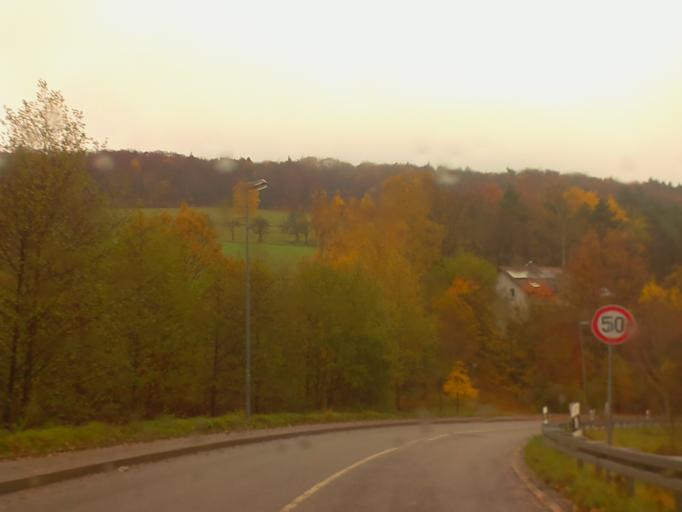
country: DE
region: Baden-Wuerttemberg
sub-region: Karlsruhe Region
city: Wilhelmsfeld
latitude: 49.4659
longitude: 8.7647
